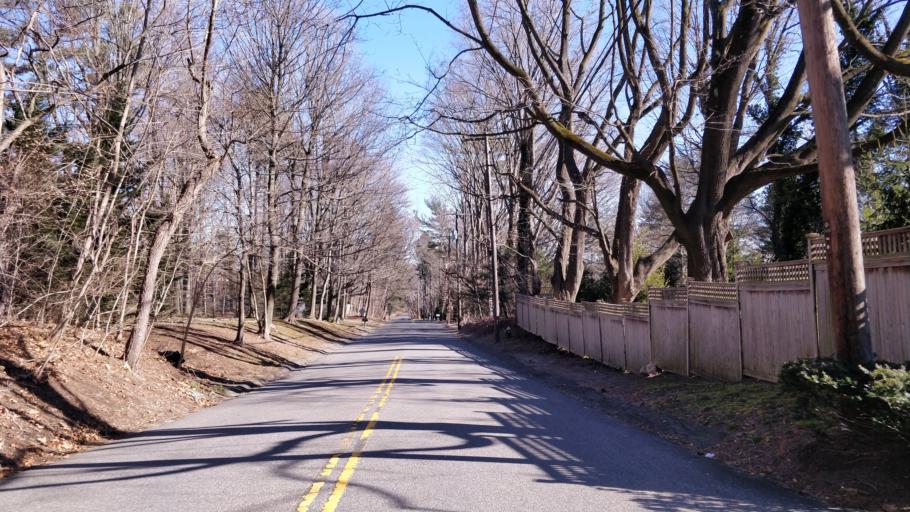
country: US
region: New York
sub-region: Nassau County
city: Glen Head
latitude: 40.8230
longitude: -73.6220
